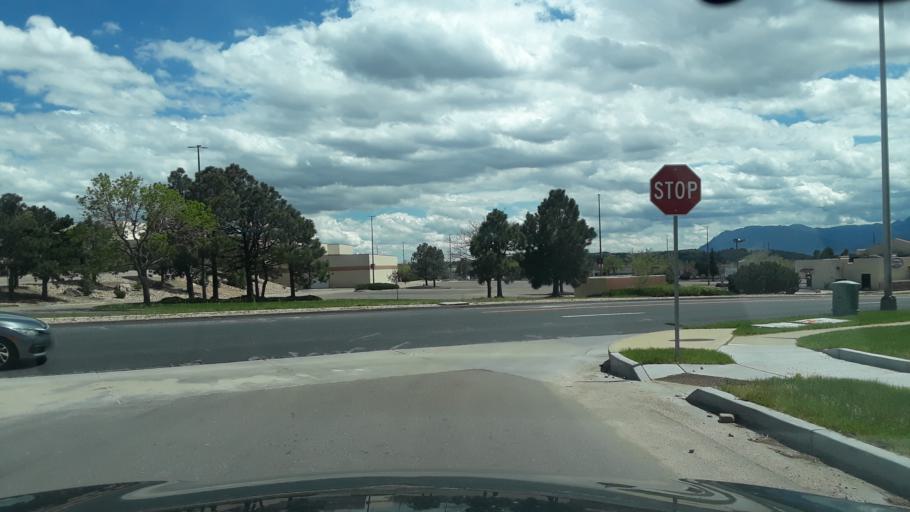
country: US
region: Colorado
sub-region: El Paso County
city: Air Force Academy
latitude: 38.9488
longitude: -104.7986
